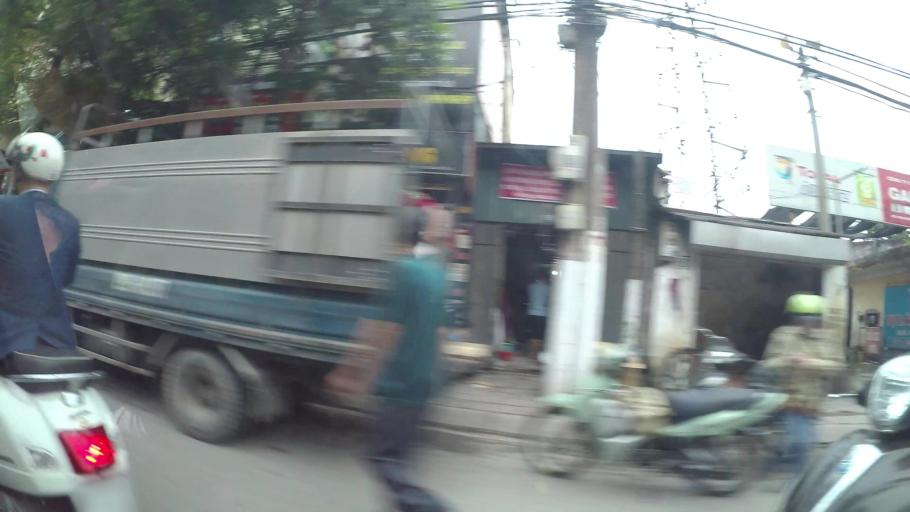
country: VN
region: Ha Noi
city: Hai BaTrung
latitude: 21.0020
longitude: 105.8701
